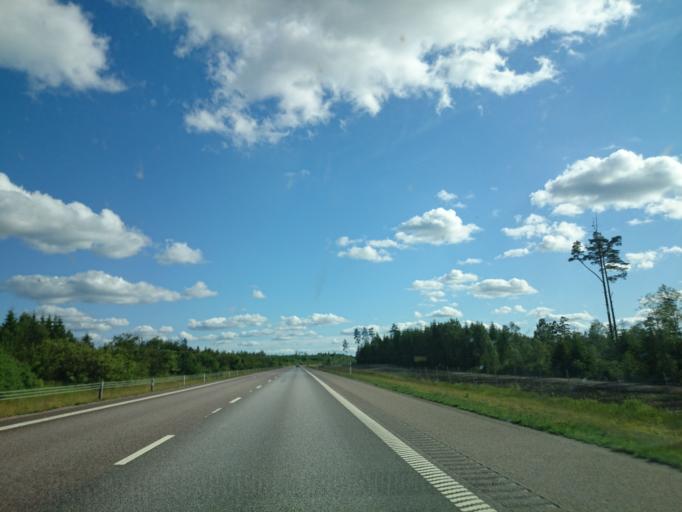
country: SE
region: Kronoberg
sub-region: Ljungby Kommun
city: Ljungby
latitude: 56.7341
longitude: 13.8505
